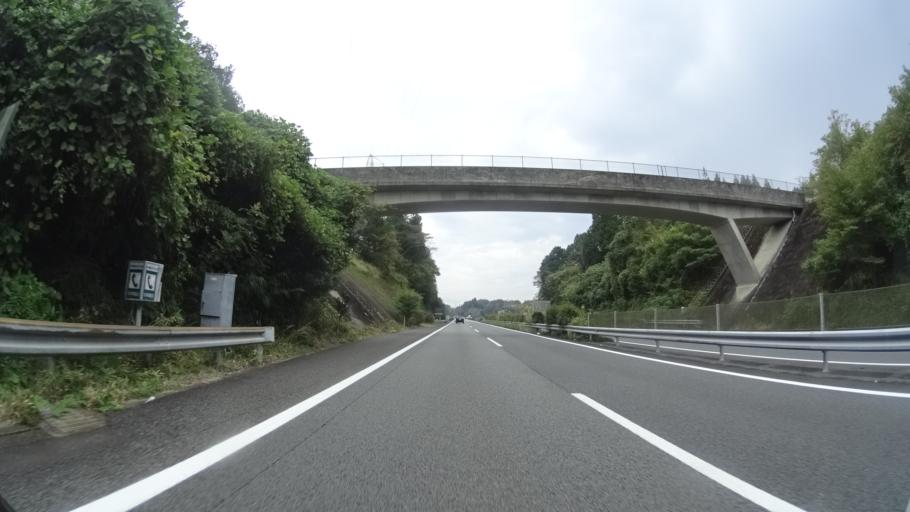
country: JP
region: Kumamoto
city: Hitoyoshi
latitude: 32.2114
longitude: 130.7746
